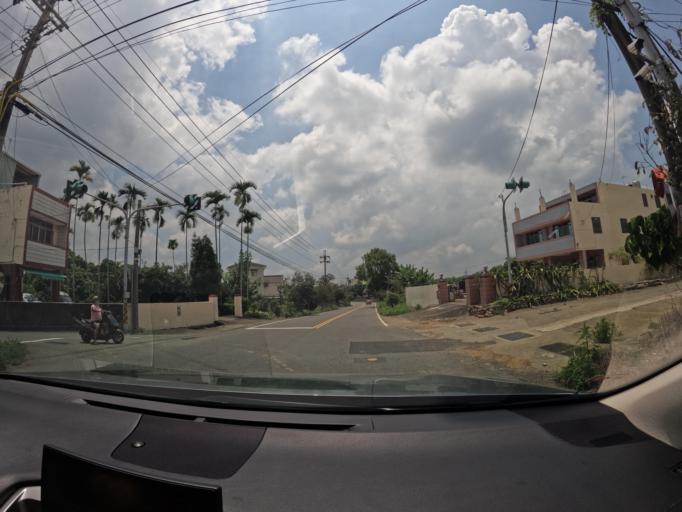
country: TW
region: Taiwan
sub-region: Nantou
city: Nantou
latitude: 23.8798
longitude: 120.6338
